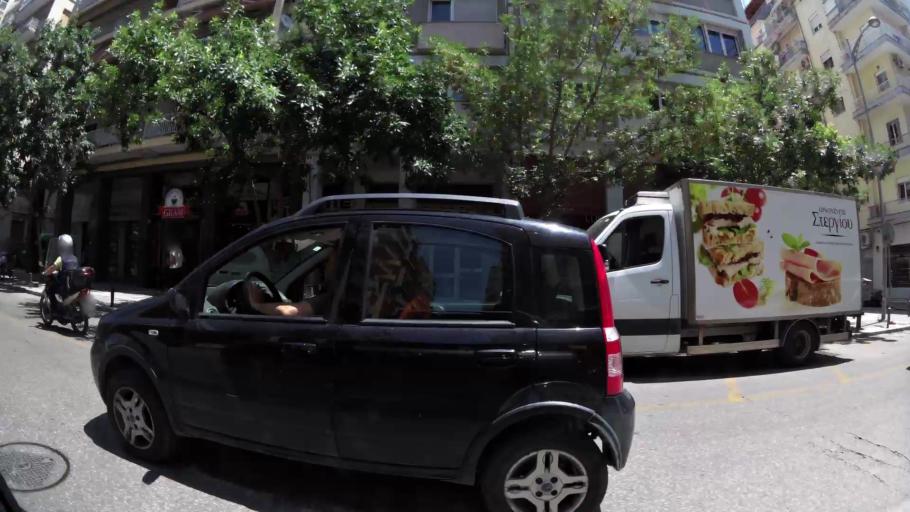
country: GR
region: Central Macedonia
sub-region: Nomos Thessalonikis
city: Triandria
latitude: 40.6084
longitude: 22.9535
